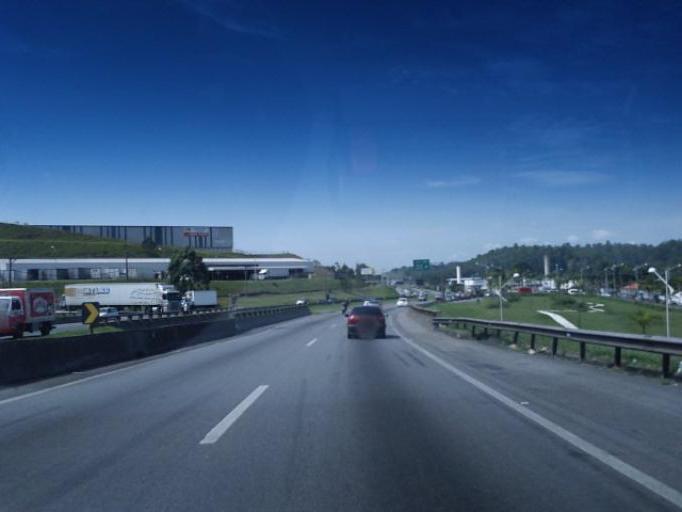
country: BR
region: Sao Paulo
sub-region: Embu
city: Embu
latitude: -23.6594
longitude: -46.8513
